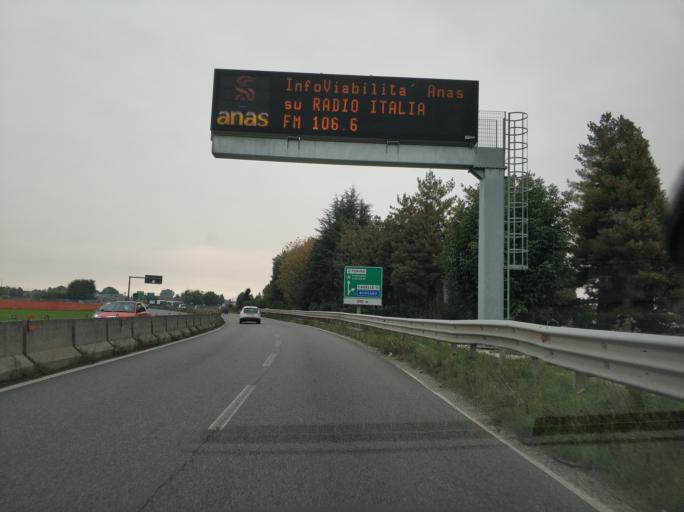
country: IT
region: Piedmont
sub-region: Provincia di Torino
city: Caselle Torinese
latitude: 45.1825
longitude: 7.6458
